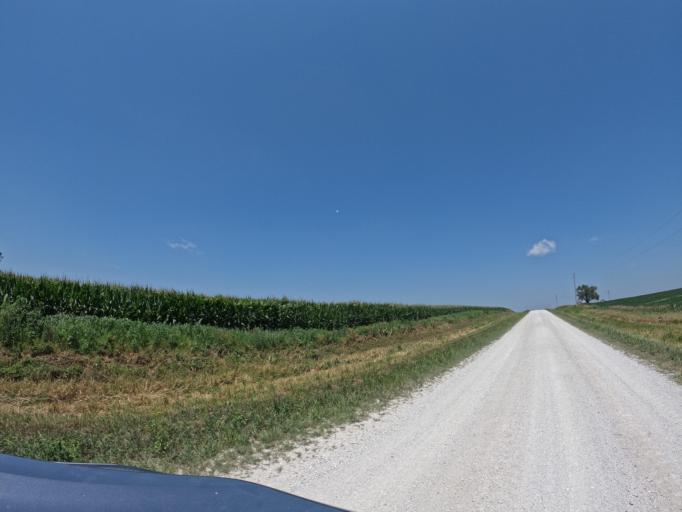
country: US
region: Iowa
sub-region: Keokuk County
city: Sigourney
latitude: 41.2628
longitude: -92.1698
